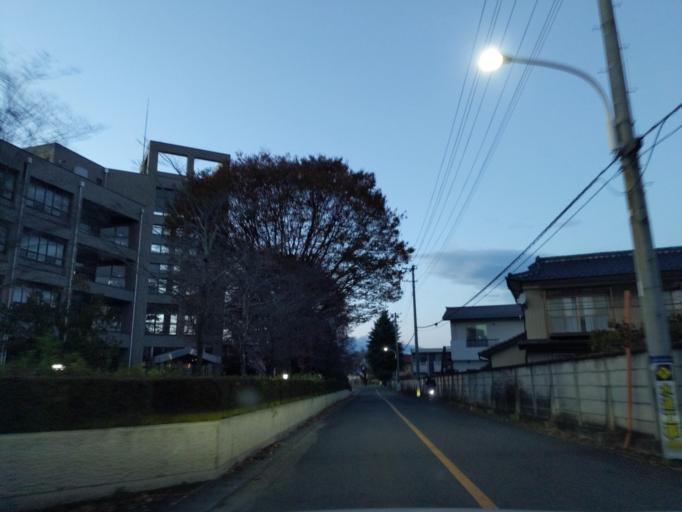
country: JP
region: Fukushima
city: Koriyama
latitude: 37.3609
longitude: 140.3835
